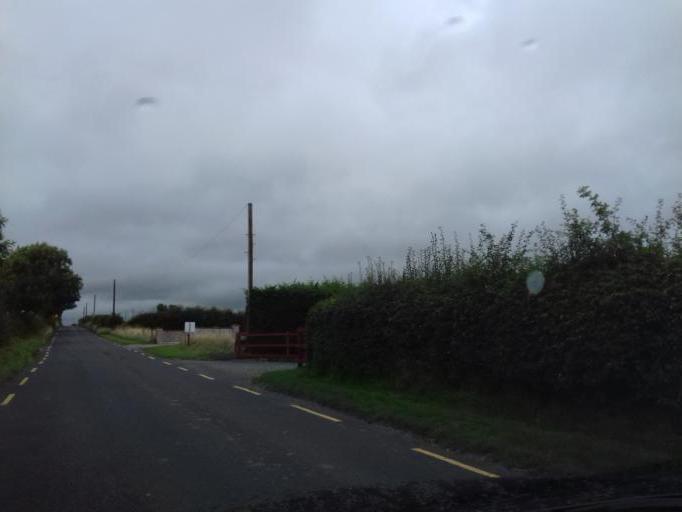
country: IE
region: Leinster
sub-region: Kilkenny
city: Graiguenamanagh
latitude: 52.6114
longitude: -7.0305
